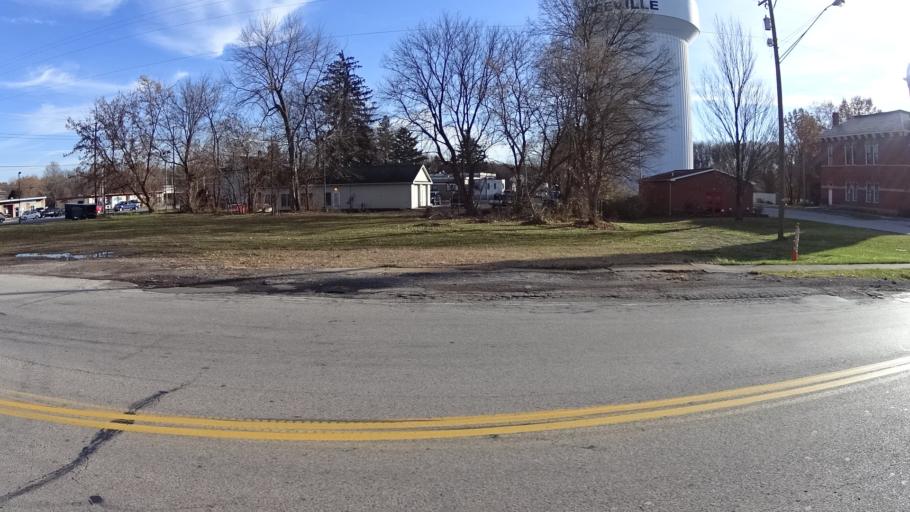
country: US
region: Ohio
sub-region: Lorain County
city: North Ridgeville
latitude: 41.3899
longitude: -82.0196
